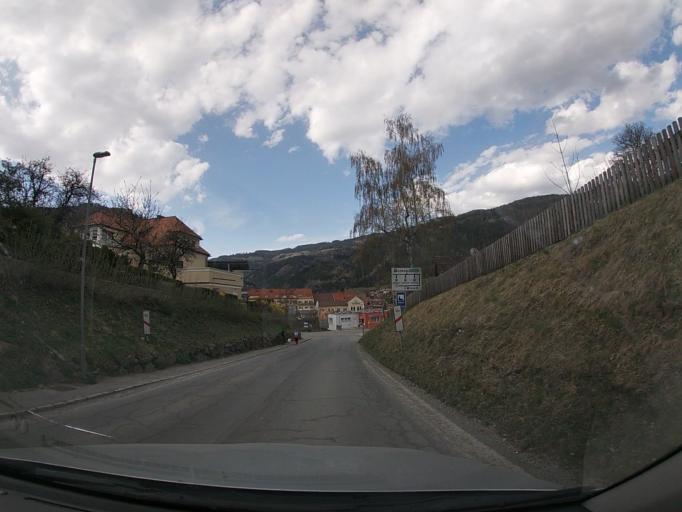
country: AT
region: Styria
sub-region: Politischer Bezirk Murau
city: Murau
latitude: 47.1084
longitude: 14.1720
